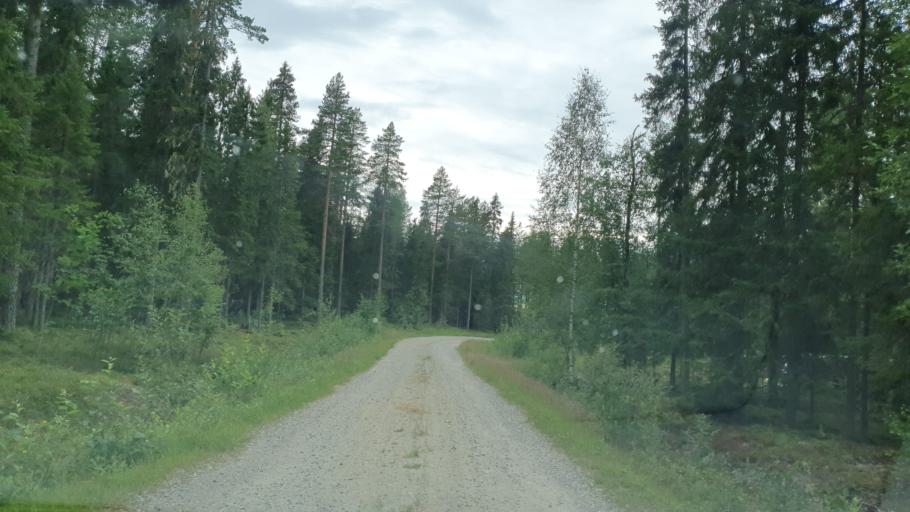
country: FI
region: Kainuu
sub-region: Kehys-Kainuu
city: Kuhmo
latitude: 64.2028
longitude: 29.3833
